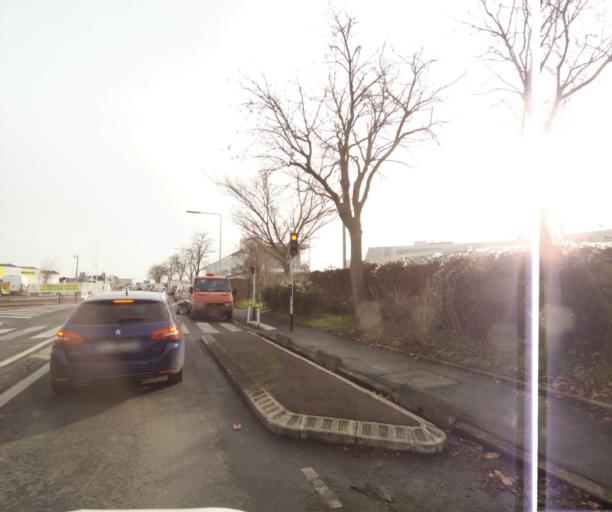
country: FR
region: Ile-de-France
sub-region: Departement du Val-d'Oise
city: Bezons
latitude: 48.9069
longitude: 2.2183
